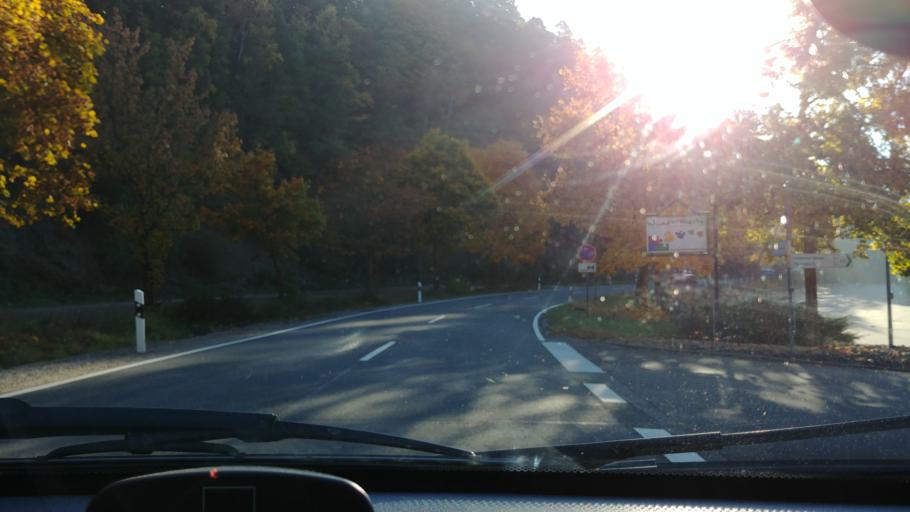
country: DE
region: Hesse
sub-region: Regierungsbezirk Darmstadt
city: Bad Schwalbach
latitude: 50.1515
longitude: 8.0679
